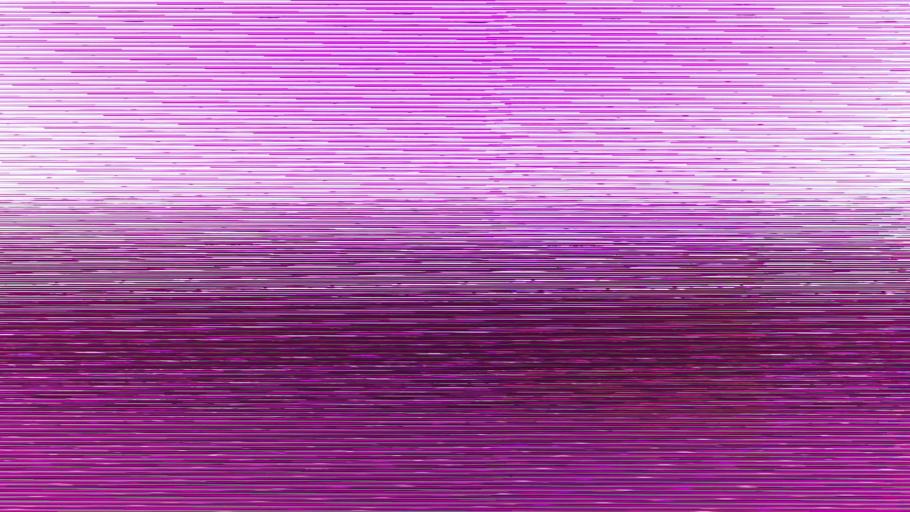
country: US
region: Michigan
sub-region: Washtenaw County
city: Ypsilanti
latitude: 42.2253
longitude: -83.6324
